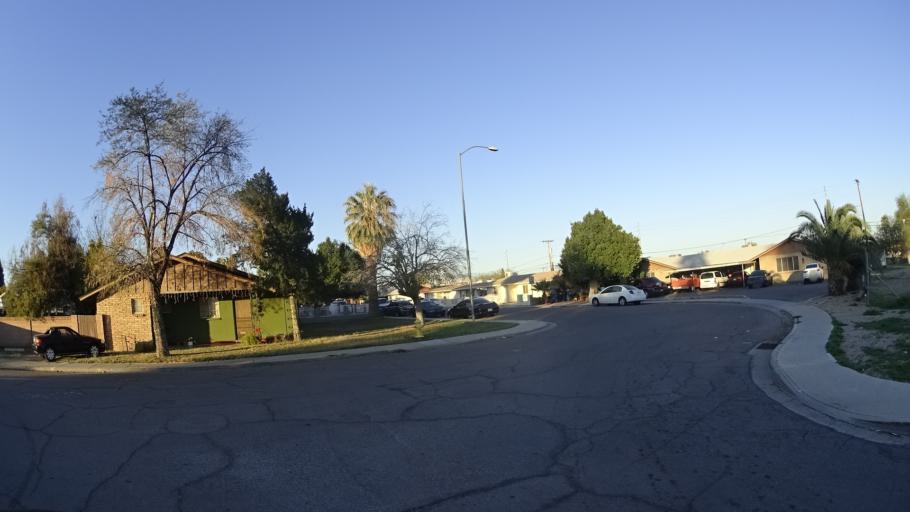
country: US
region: Arizona
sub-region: Maricopa County
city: Mesa
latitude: 33.4230
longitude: -111.8326
